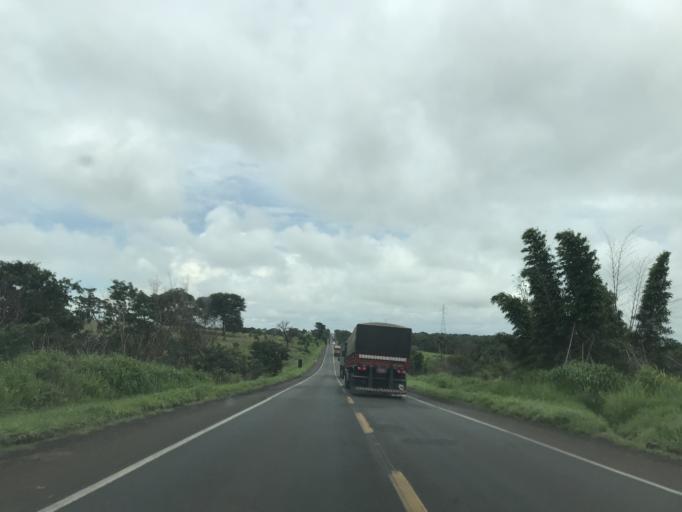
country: BR
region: Minas Gerais
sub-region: Frutal
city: Frutal
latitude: -19.8007
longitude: -48.9673
